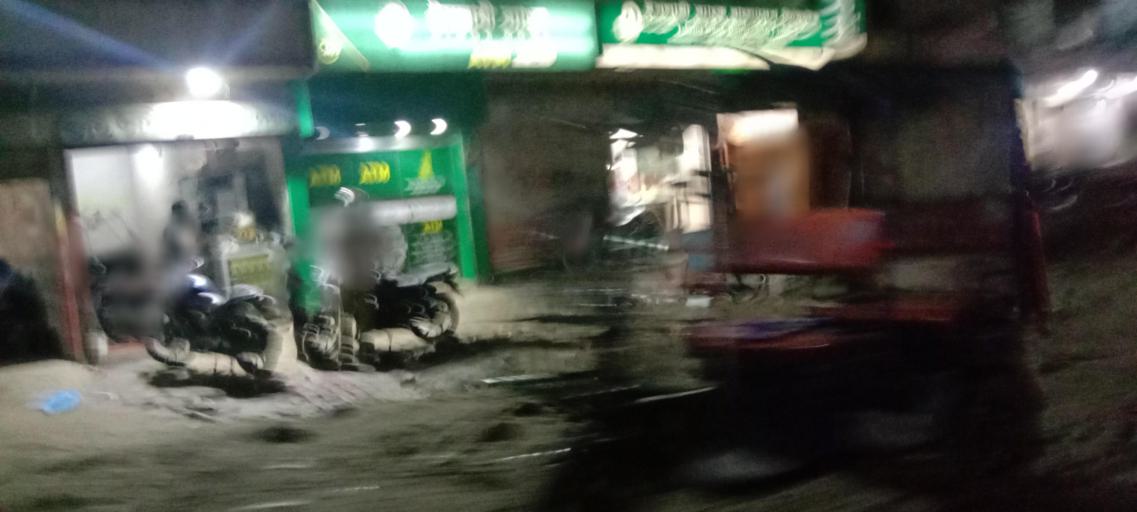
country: BD
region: Dhaka
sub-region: Dhaka
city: Dhaka
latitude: 23.7001
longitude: 90.3805
